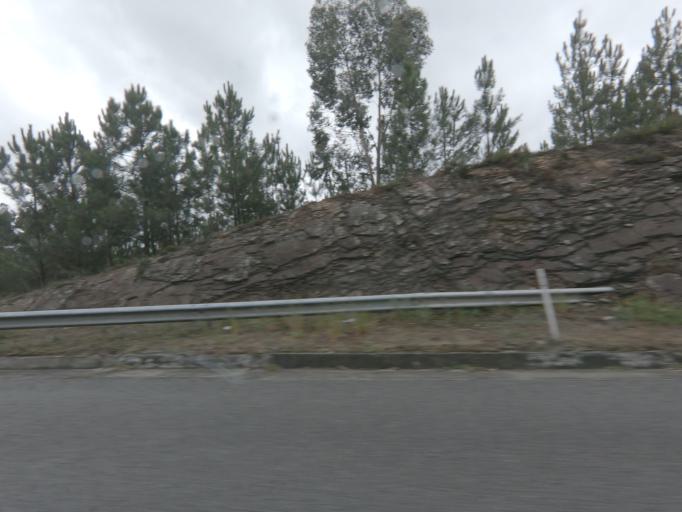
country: PT
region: Porto
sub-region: Paredes
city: Recarei
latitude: 41.1666
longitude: -8.4039
